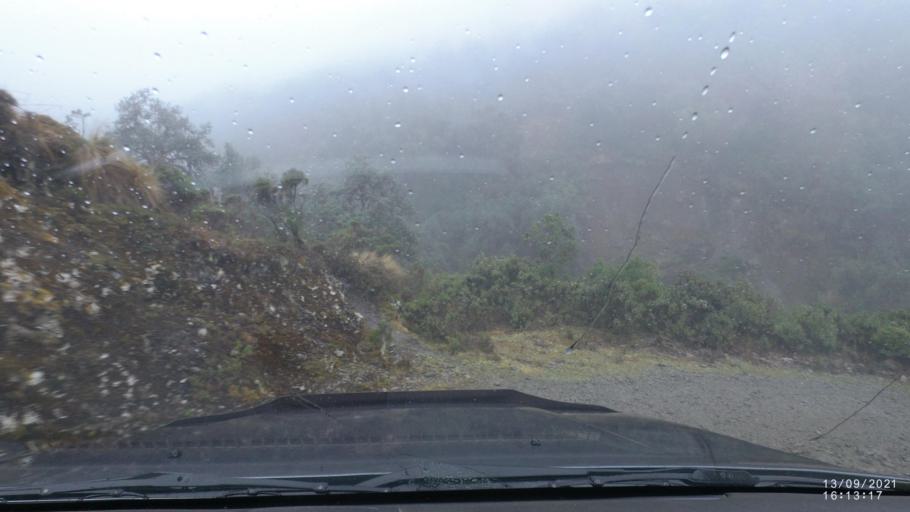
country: BO
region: Cochabamba
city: Colomi
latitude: -17.2797
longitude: -65.7144
